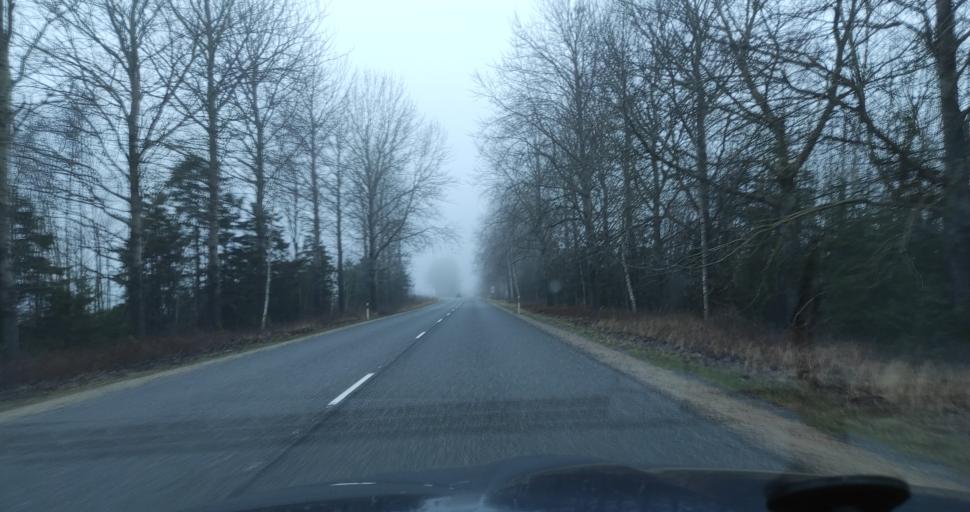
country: LV
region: Alsunga
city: Alsunga
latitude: 56.9956
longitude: 21.3730
